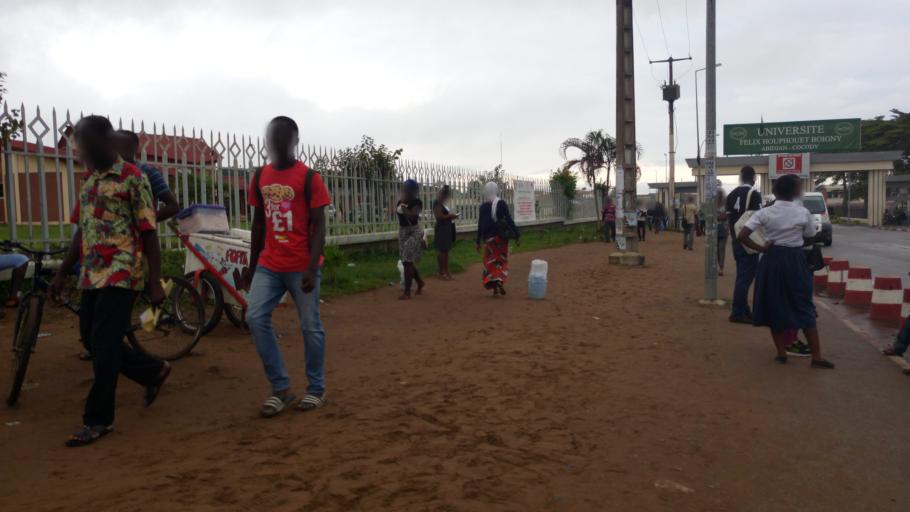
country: CI
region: Lagunes
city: Abidjan
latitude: 5.3498
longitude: -3.9886
